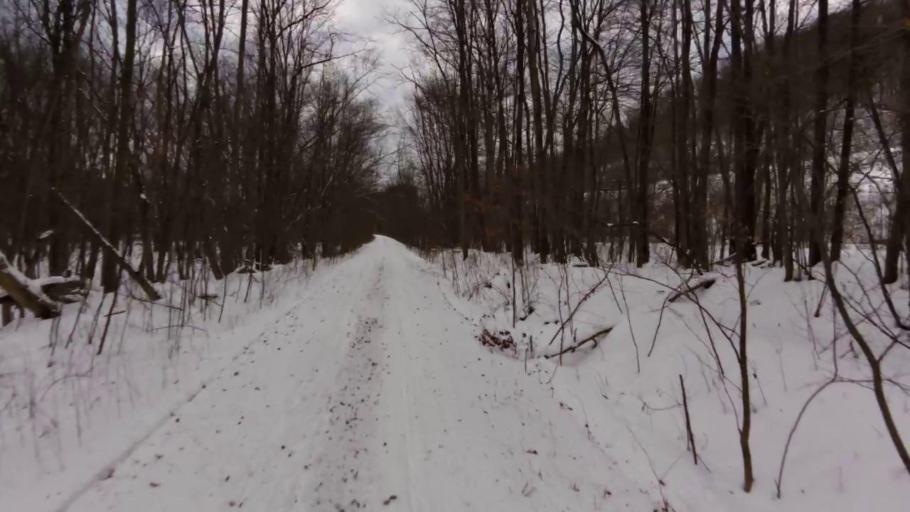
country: US
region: Pennsylvania
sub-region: McKean County
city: Foster Brook
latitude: 42.0589
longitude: -78.6376
